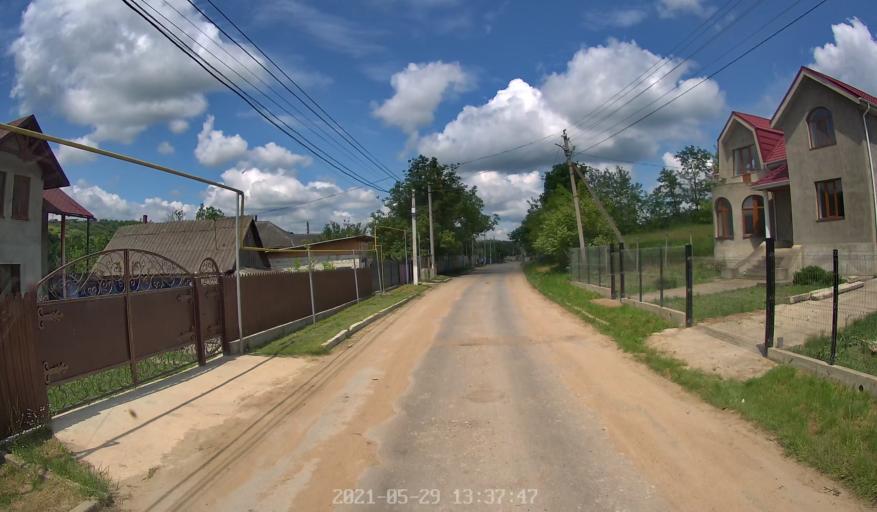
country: MD
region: Hincesti
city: Hincesti
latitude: 46.8288
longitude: 28.6765
